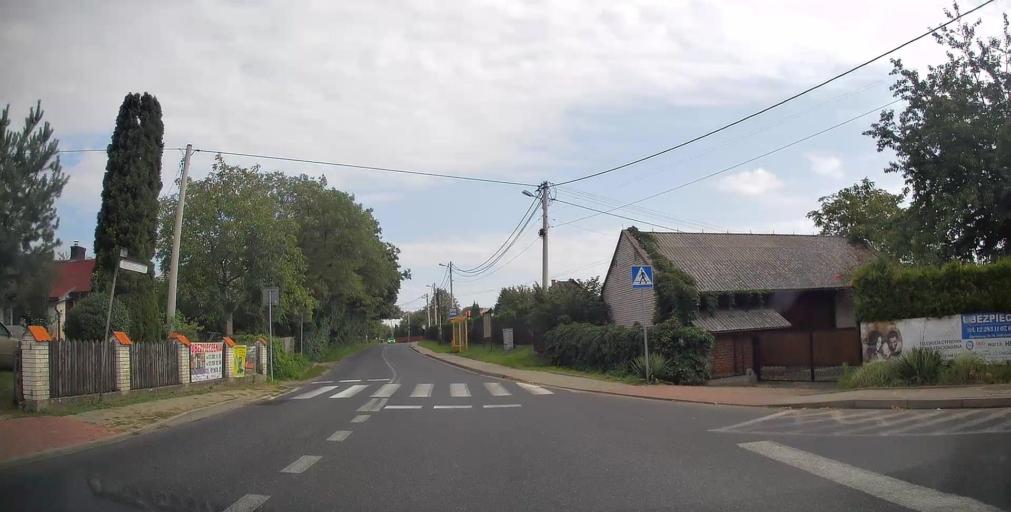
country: PL
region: Lesser Poland Voivodeship
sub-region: Powiat chrzanowski
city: Grojec
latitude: 50.0901
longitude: 19.5562
